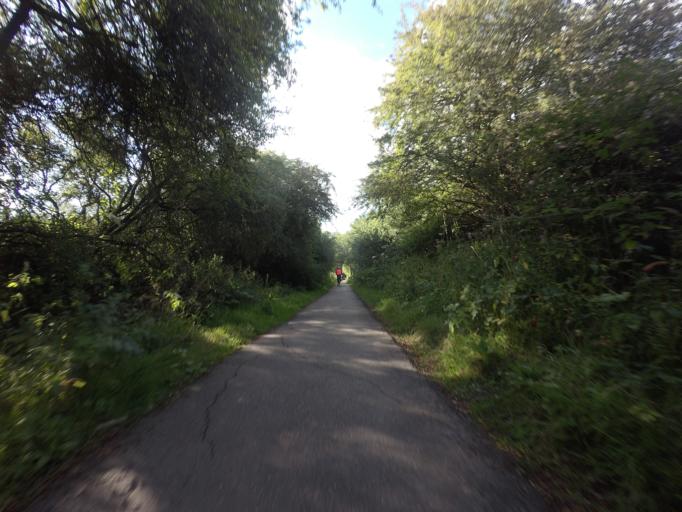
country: GB
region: England
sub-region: East Sussex
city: Horam
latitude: 50.9170
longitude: 0.2572
